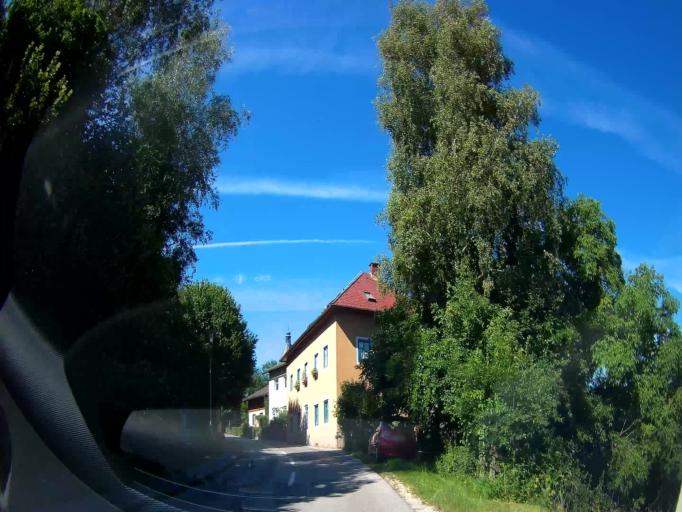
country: AT
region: Carinthia
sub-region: Politischer Bezirk Klagenfurt Land
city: Maria Saal
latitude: 46.6822
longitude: 14.3481
